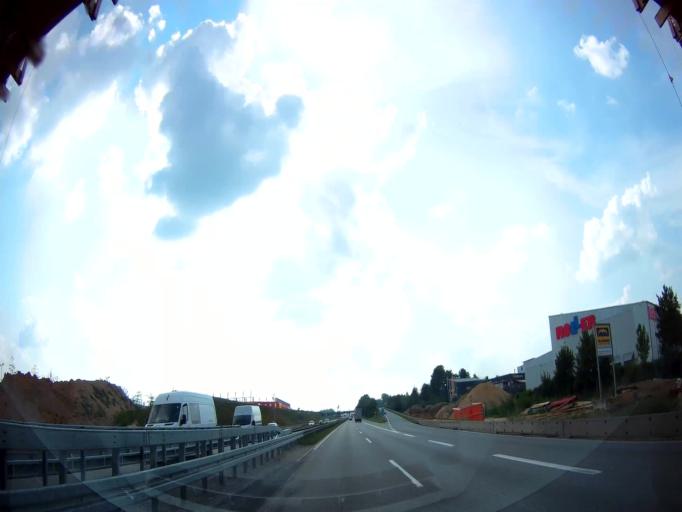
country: DE
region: Bavaria
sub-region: Upper Palatinate
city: Regensburg
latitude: 48.9915
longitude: 12.1129
